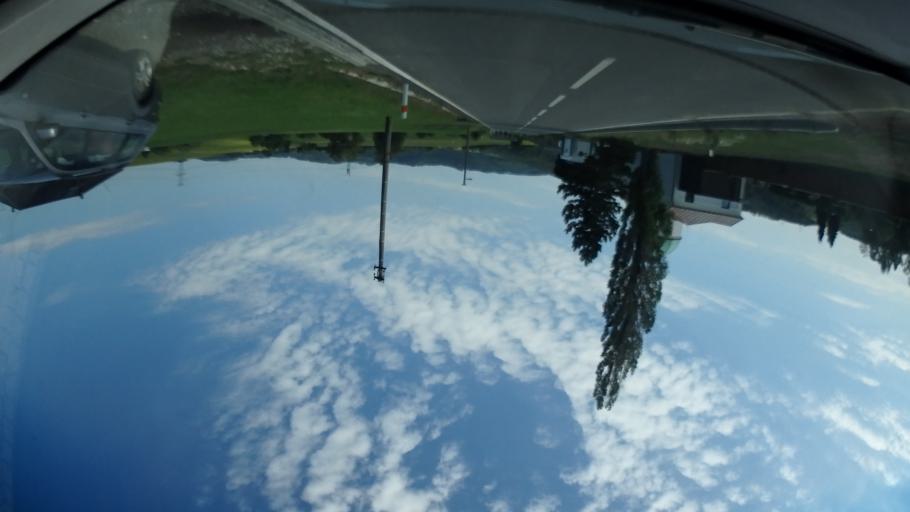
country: CZ
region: Olomoucky
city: Zabreh
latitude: 49.8802
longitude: 16.8594
